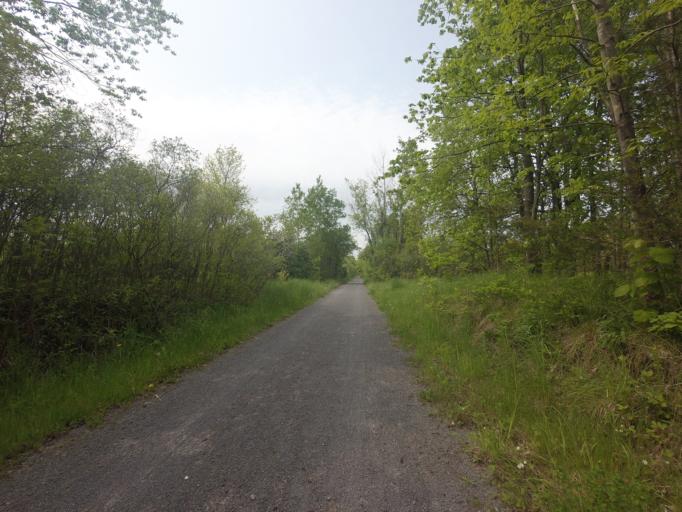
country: CA
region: Ontario
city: Kingston
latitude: 44.3230
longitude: -76.5877
